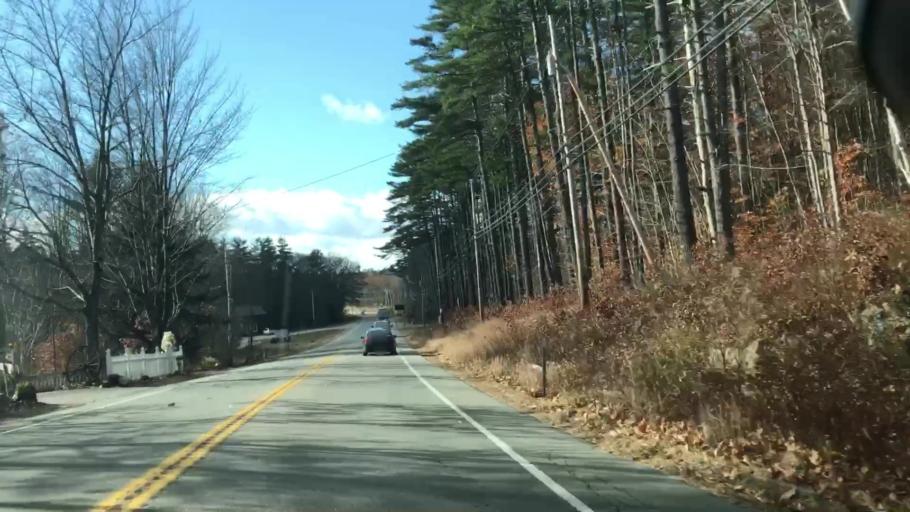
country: US
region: New Hampshire
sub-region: Carroll County
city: Wolfeboro
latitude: 43.6104
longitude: -71.1793
